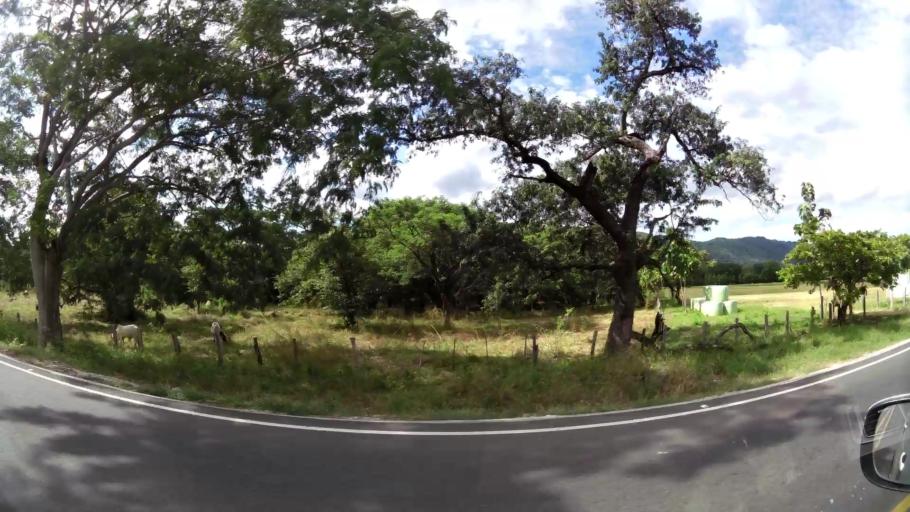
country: CR
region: Guanacaste
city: Hojancha
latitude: 10.1389
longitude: -85.3363
